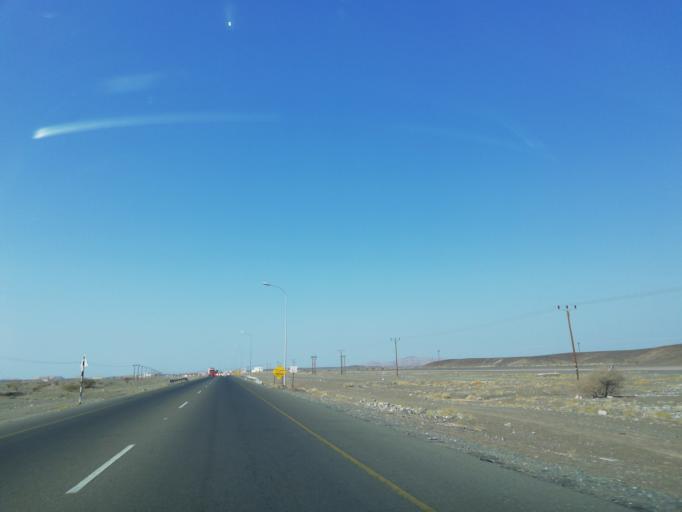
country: OM
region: Ash Sharqiyah
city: Ibra'
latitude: 22.7132
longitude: 58.1451
